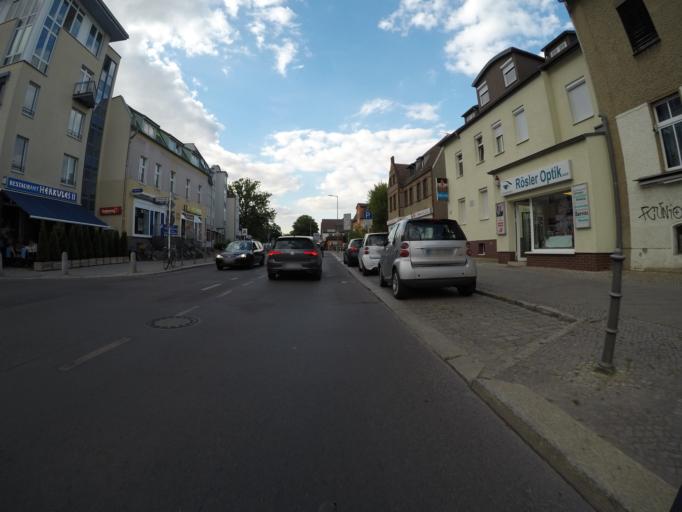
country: DE
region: Berlin
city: Mahlsdorf
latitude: 52.5130
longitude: 13.6123
